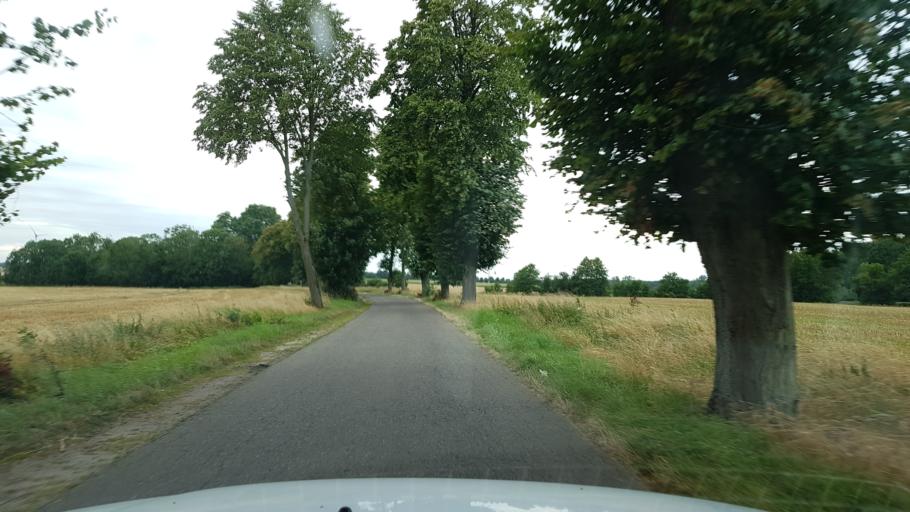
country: PL
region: West Pomeranian Voivodeship
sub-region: Powiat bialogardzki
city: Karlino
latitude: 54.1159
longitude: 15.8684
